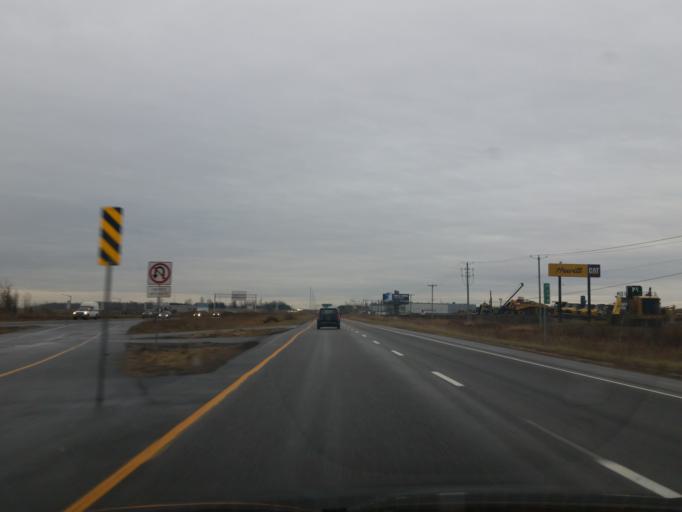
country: CA
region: Quebec
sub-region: Capitale-Nationale
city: Saint-Augustin-de-Desmaures
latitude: 46.7596
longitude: -71.4427
